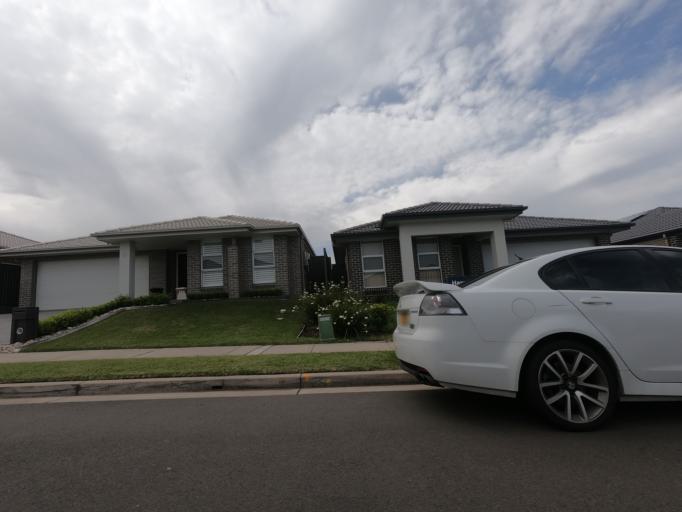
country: AU
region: New South Wales
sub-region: Wollongong
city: Dapto
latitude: -34.4958
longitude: 150.7605
